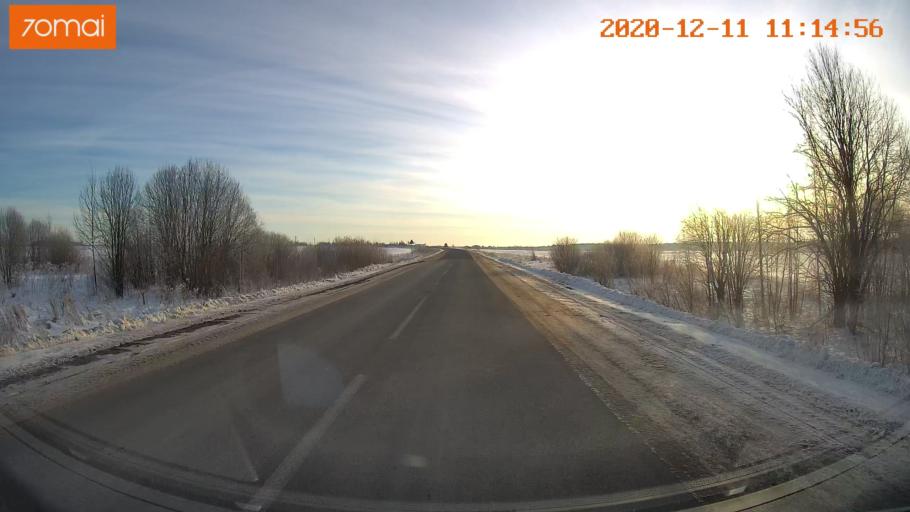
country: RU
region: Jaroslavl
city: Lyubim
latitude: 58.3217
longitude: 40.9233
